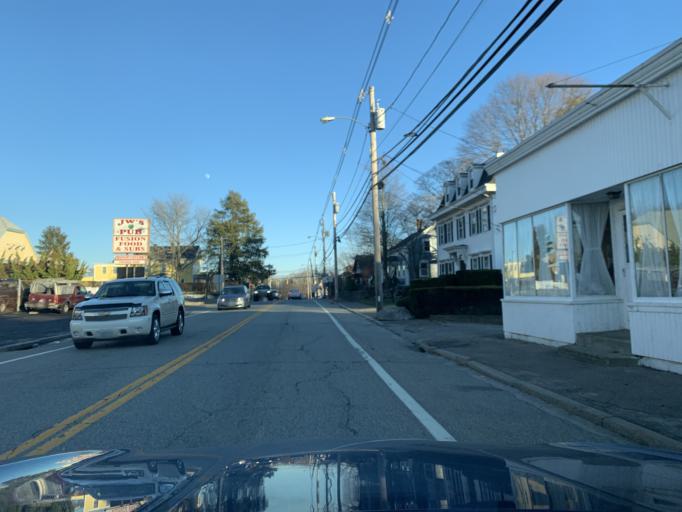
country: US
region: Rhode Island
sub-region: Kent County
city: West Warwick
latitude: 41.6955
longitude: -71.5364
